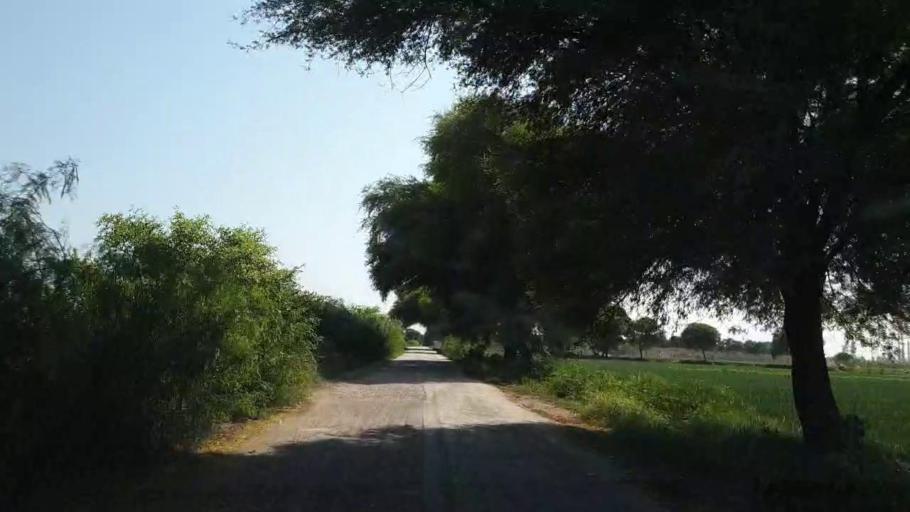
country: PK
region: Sindh
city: Tando Jam
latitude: 25.3935
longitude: 68.5870
